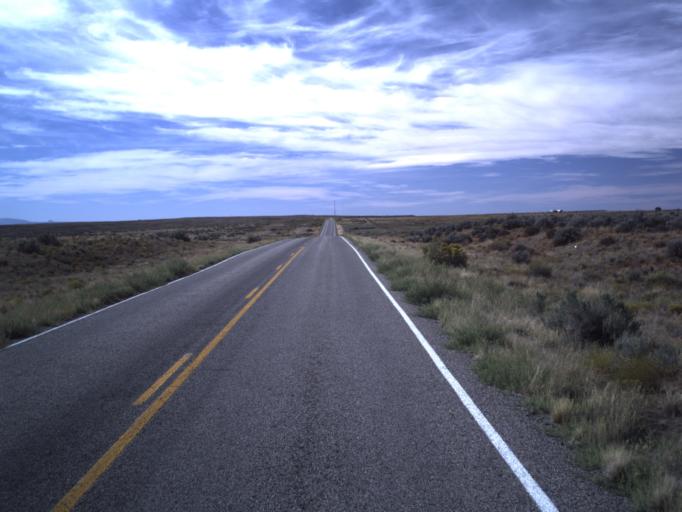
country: US
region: Utah
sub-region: San Juan County
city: Blanding
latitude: 37.3609
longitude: -109.3453
